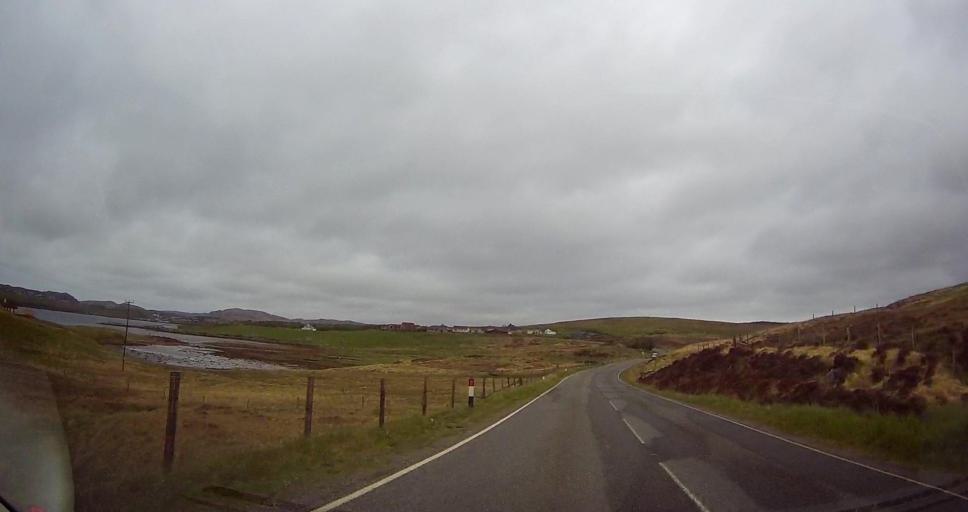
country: GB
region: Scotland
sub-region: Shetland Islands
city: Lerwick
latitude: 60.3809
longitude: -1.3425
